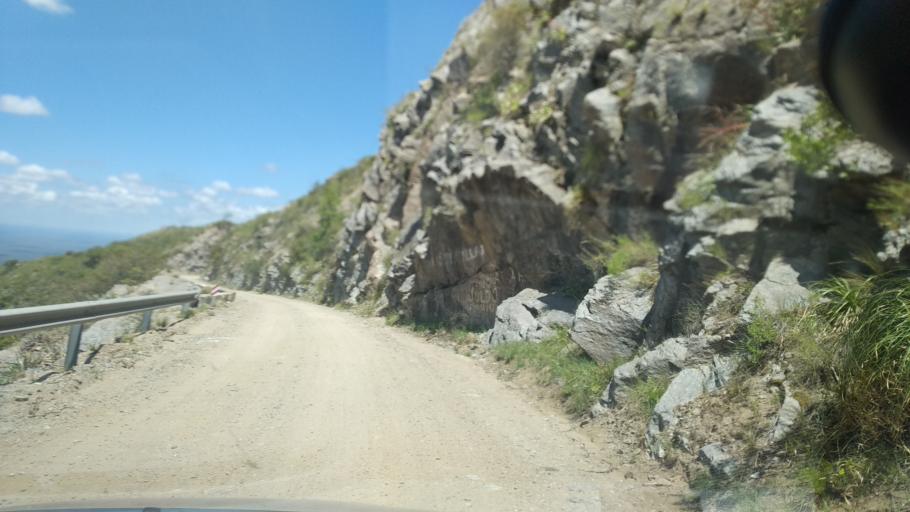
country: AR
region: Cordoba
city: Salsacate
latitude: -31.3785
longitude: -65.3983
